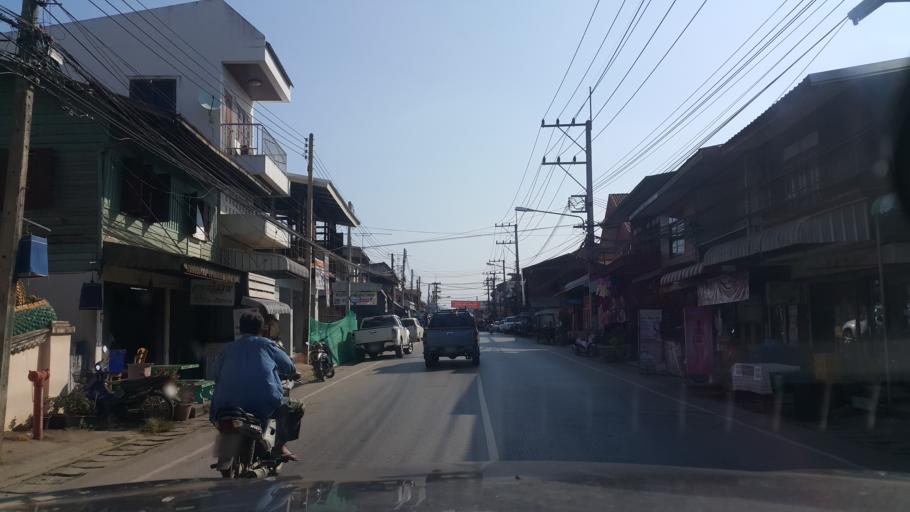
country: TH
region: Loei
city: Chiang Khan
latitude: 17.8950
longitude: 101.6574
